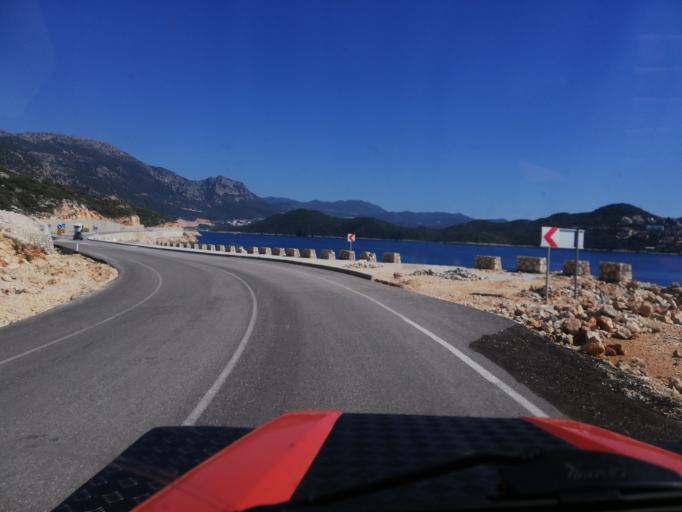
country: TR
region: Antalya
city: Kas
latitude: 36.2014
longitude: 29.5854
